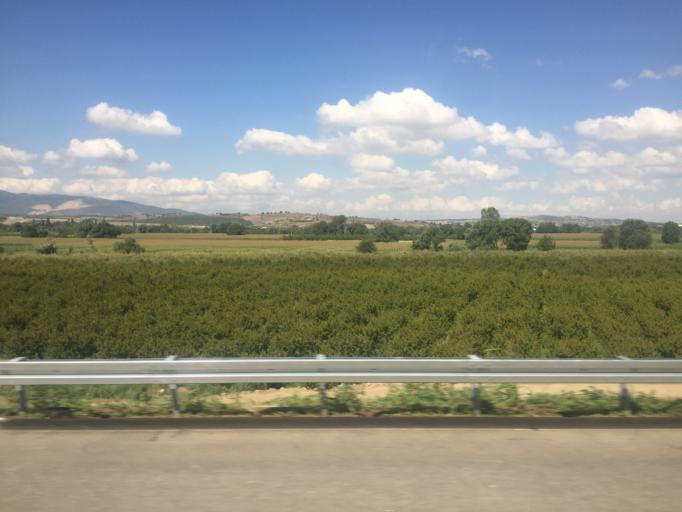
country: TR
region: Balikesir
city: Gobel
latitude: 39.9995
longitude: 28.1927
